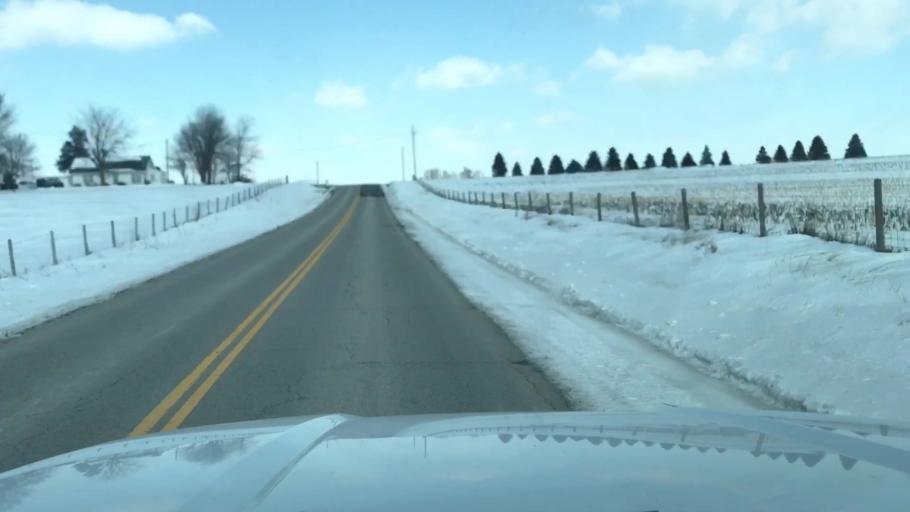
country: US
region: Missouri
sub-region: Nodaway County
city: Maryville
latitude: 40.3610
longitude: -94.7219
